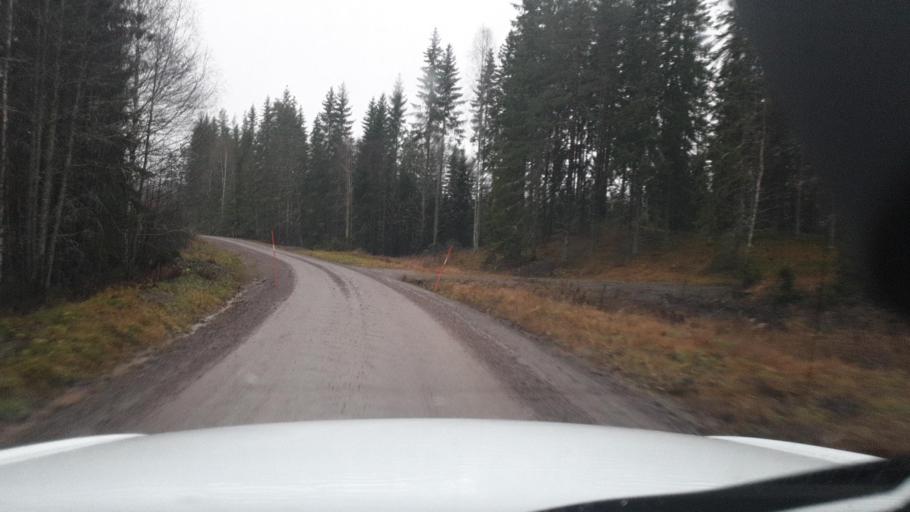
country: SE
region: Vaermland
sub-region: Arvika Kommun
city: Arvika
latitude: 59.9503
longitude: 12.6604
